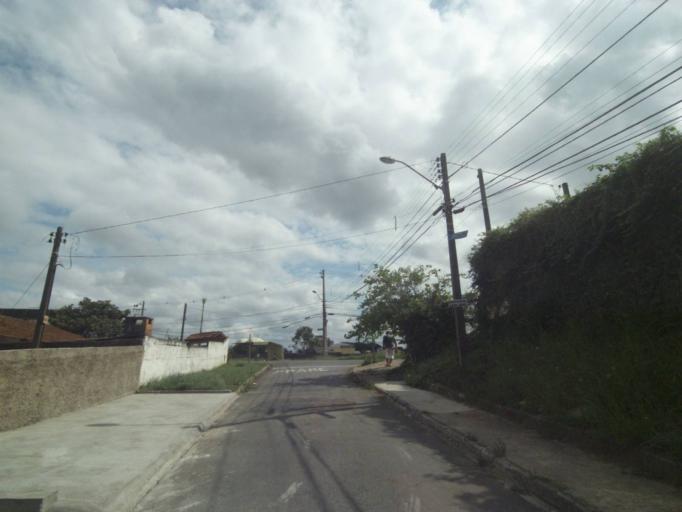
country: BR
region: Parana
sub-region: Curitiba
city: Curitiba
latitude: -25.3805
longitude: -49.2905
